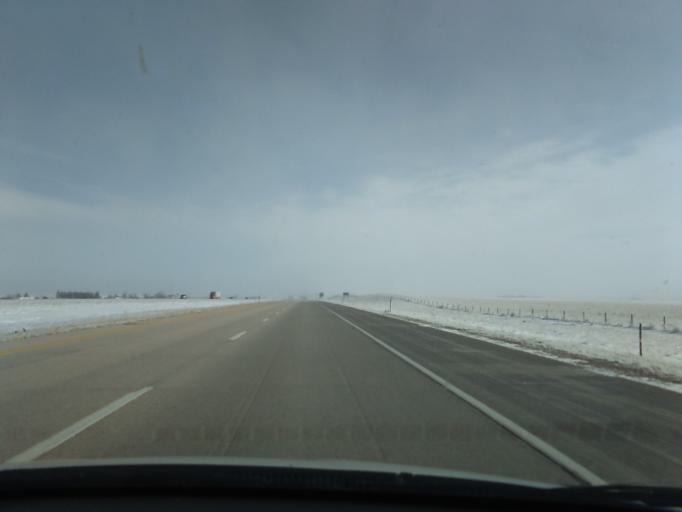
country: US
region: Wyoming
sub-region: Laramie County
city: Pine Bluffs
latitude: 41.1574
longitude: -104.3794
